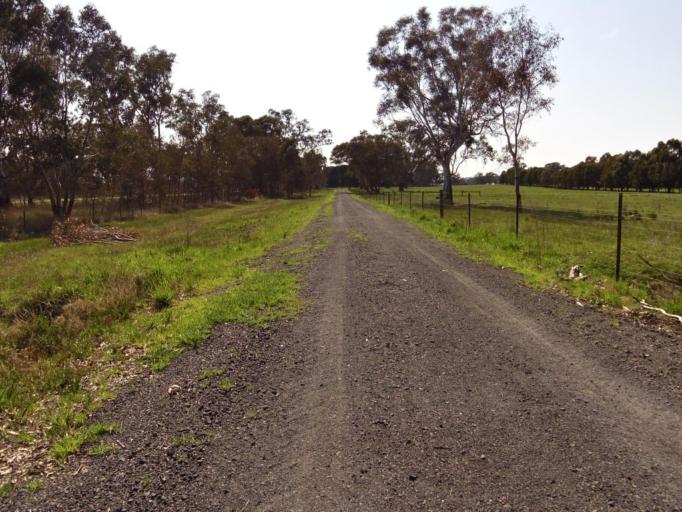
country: AU
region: Victoria
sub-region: Murrindindi
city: Alexandra
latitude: -37.1141
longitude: 145.6076
